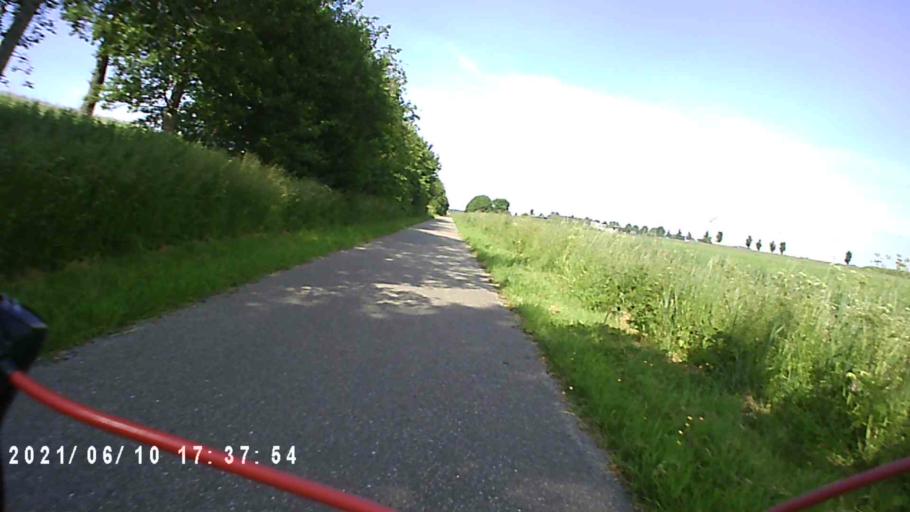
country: NL
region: Groningen
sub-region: Gemeente De Marne
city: Ulrum
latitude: 53.3229
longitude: 6.2769
